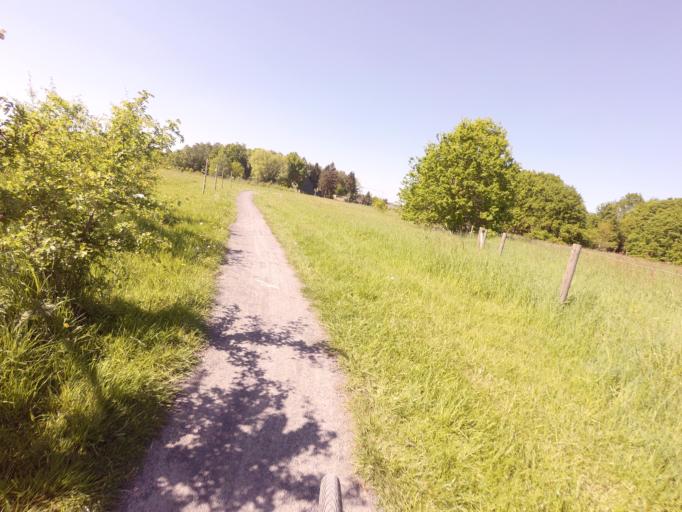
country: BE
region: Flanders
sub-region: Provincie Antwerpen
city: Borsbeek
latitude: 51.1884
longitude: 4.4981
